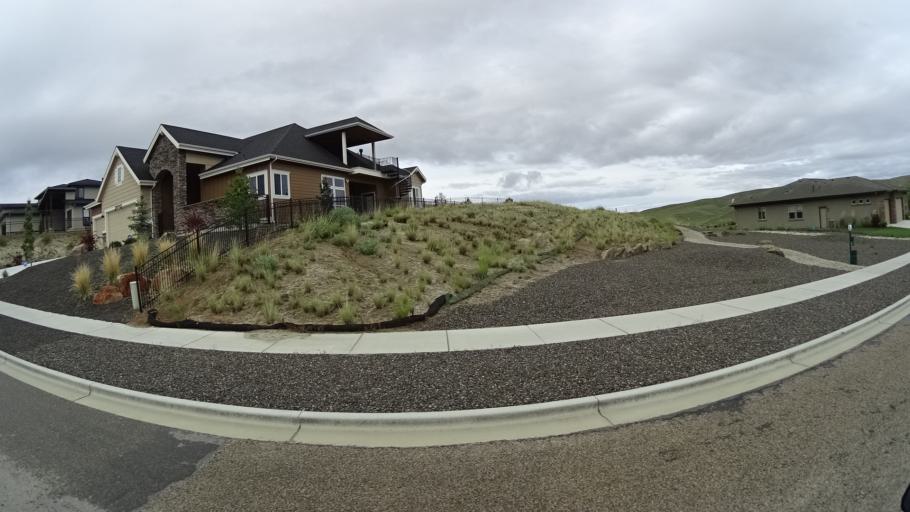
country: US
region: Idaho
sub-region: Ada County
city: Eagle
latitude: 43.7704
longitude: -116.2541
